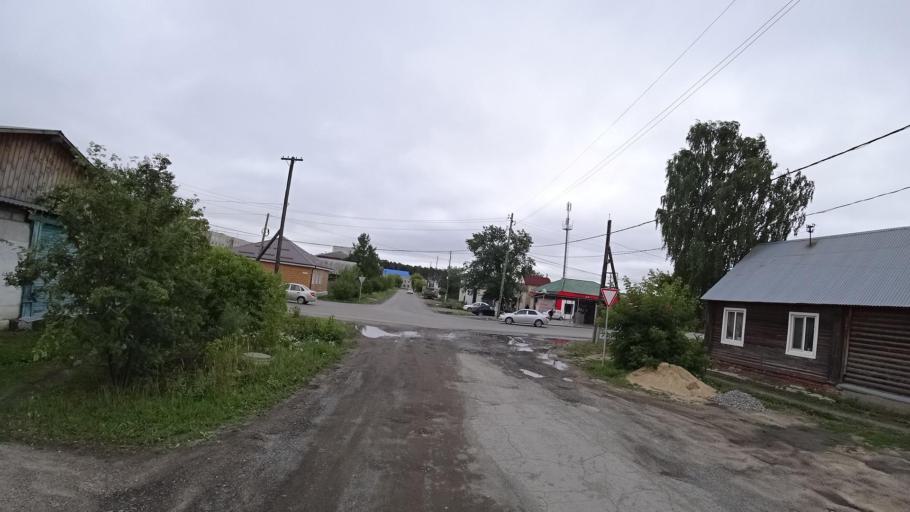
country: RU
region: Sverdlovsk
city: Kamyshlov
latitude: 56.8393
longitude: 62.7307
